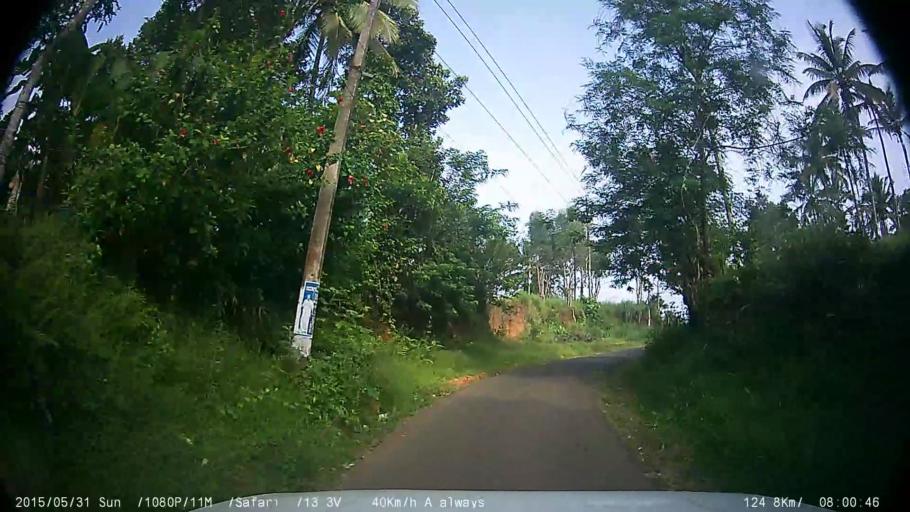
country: IN
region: Kerala
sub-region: Wayanad
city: Kalpetta
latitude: 11.6320
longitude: 76.0502
